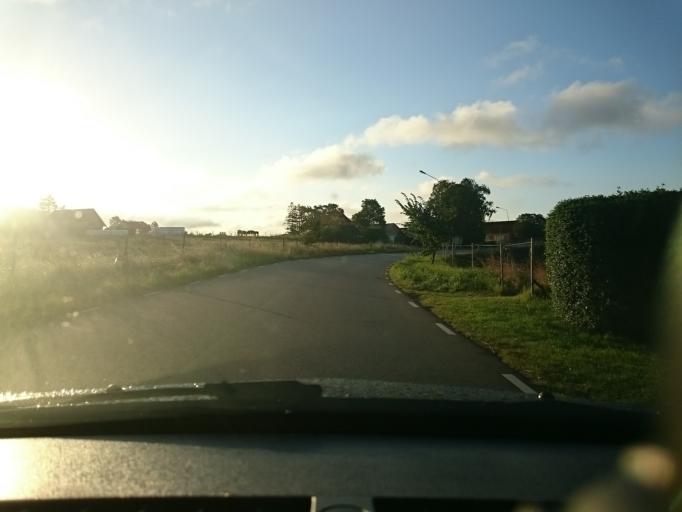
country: SE
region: Skane
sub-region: Kavlinge Kommun
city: Hofterup
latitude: 55.7875
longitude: 12.9730
